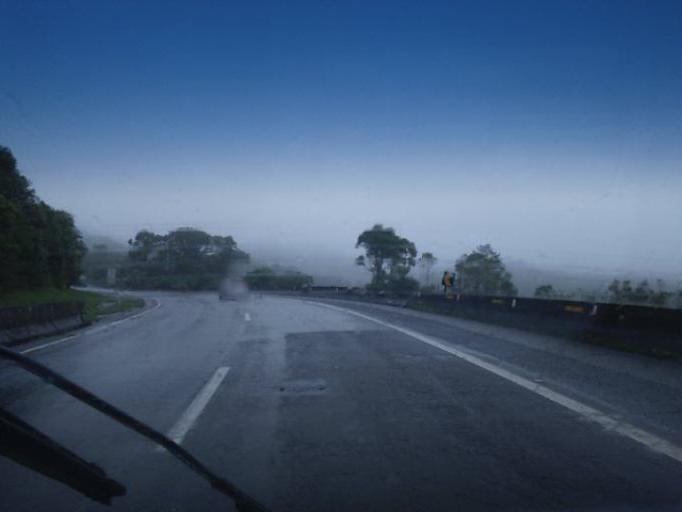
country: BR
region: Parana
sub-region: Antonina
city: Antonina
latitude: -25.1139
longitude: -48.7596
